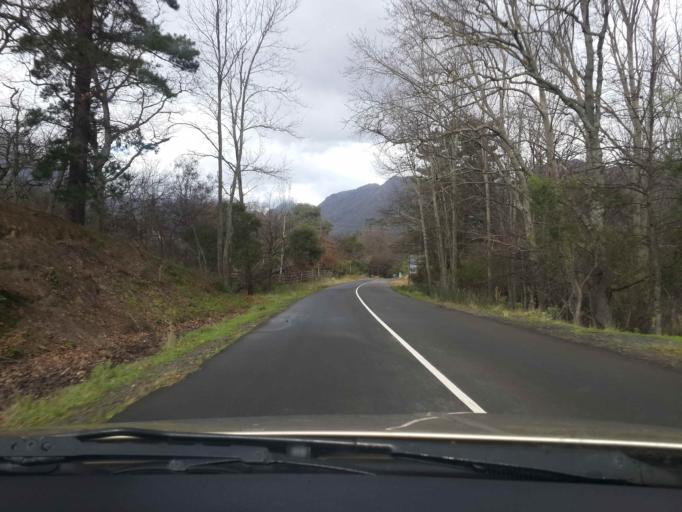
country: ZA
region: Western Cape
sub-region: Cape Winelands District Municipality
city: Stellenbosch
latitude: -33.9661
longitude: 18.9322
